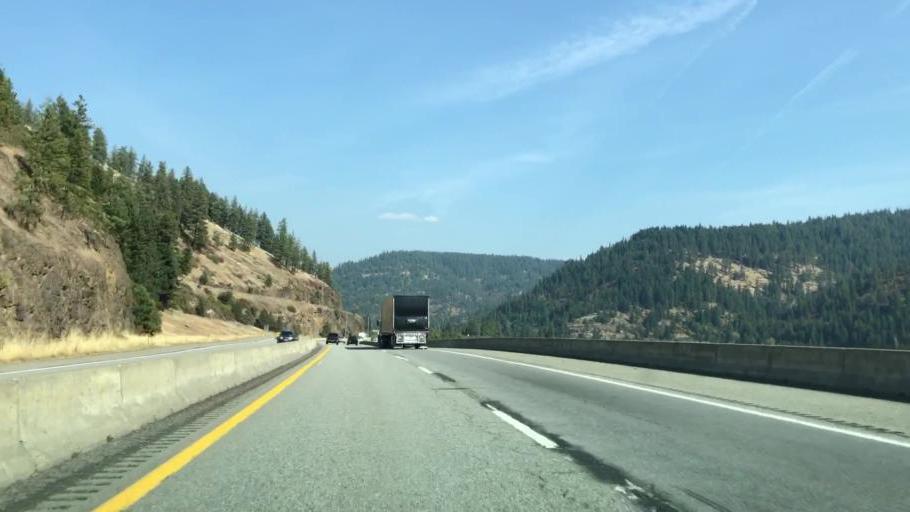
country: US
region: Idaho
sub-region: Kootenai County
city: Coeur d'Alene
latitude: 47.6235
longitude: -116.6609
